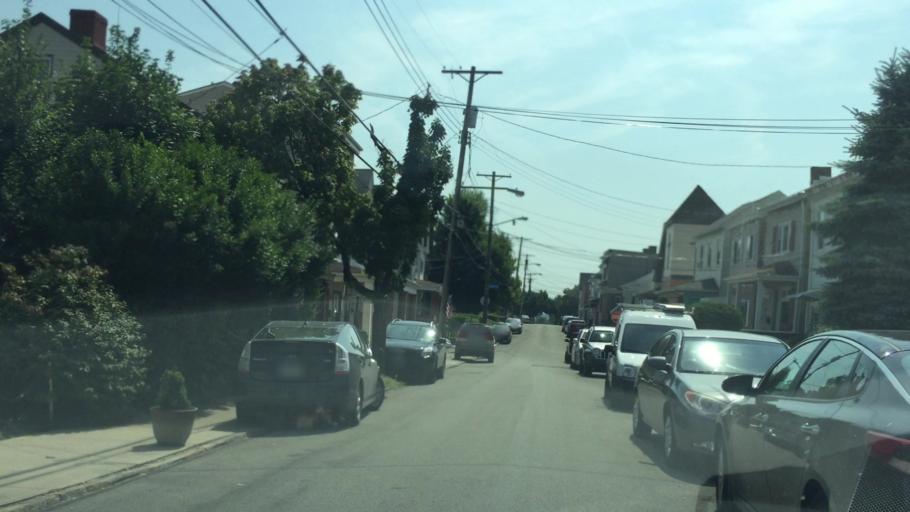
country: US
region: Pennsylvania
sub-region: Allegheny County
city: Mount Oliver
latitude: 40.4201
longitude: -79.9716
